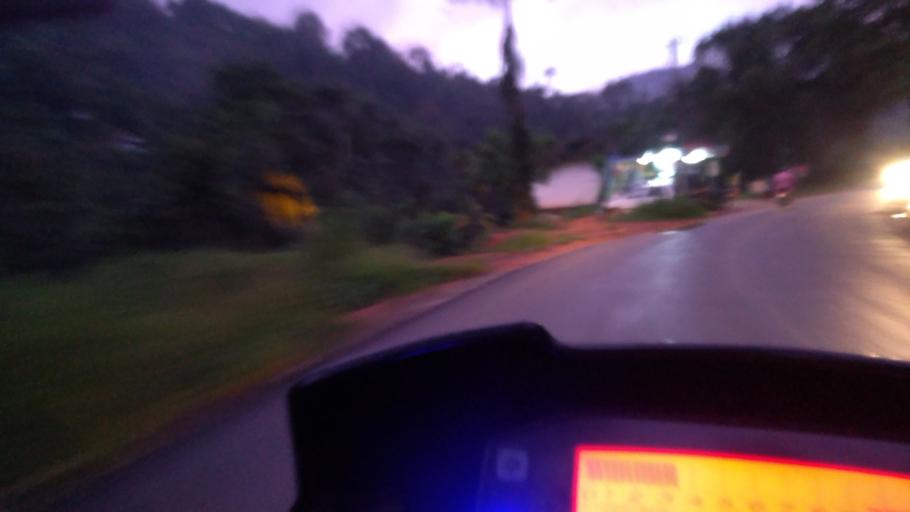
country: IN
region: Kerala
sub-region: Idukki
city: Munnar
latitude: 9.9723
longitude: 77.0589
